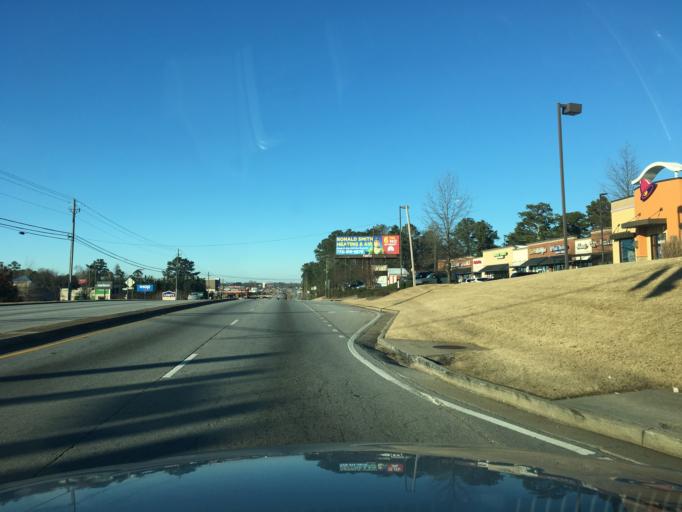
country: US
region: Georgia
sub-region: Carroll County
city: Carrollton
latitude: 33.5442
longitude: -85.0737
